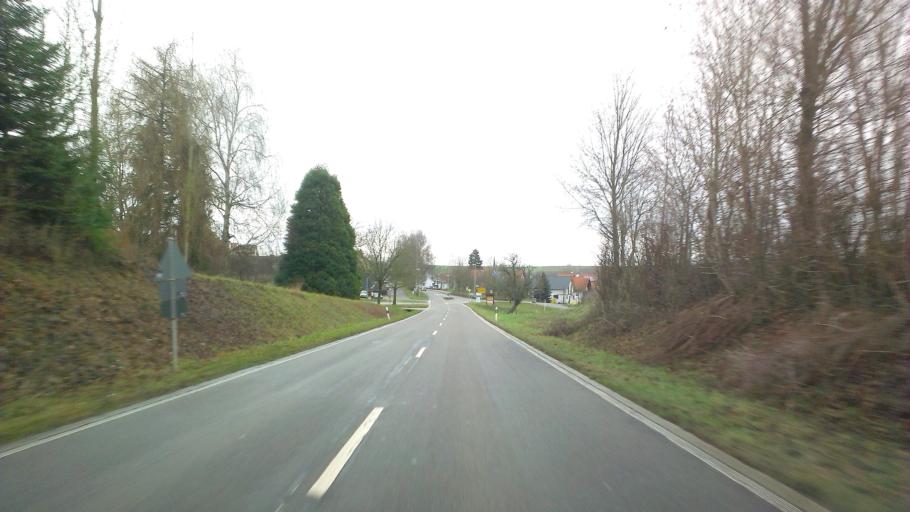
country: DE
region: Baden-Wuerttemberg
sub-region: Karlsruhe Region
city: Kurnbach
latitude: 49.0718
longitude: 8.8490
